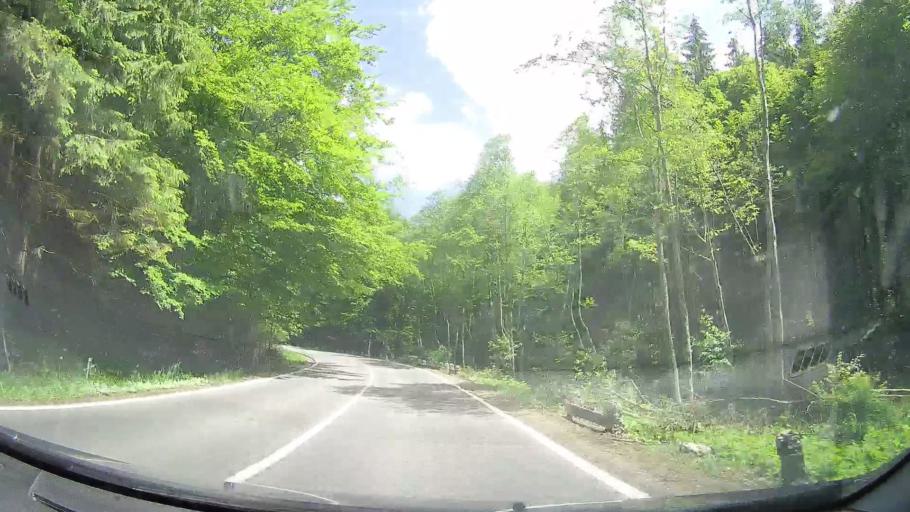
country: RO
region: Brasov
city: Crivina
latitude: 45.4590
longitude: 25.9533
